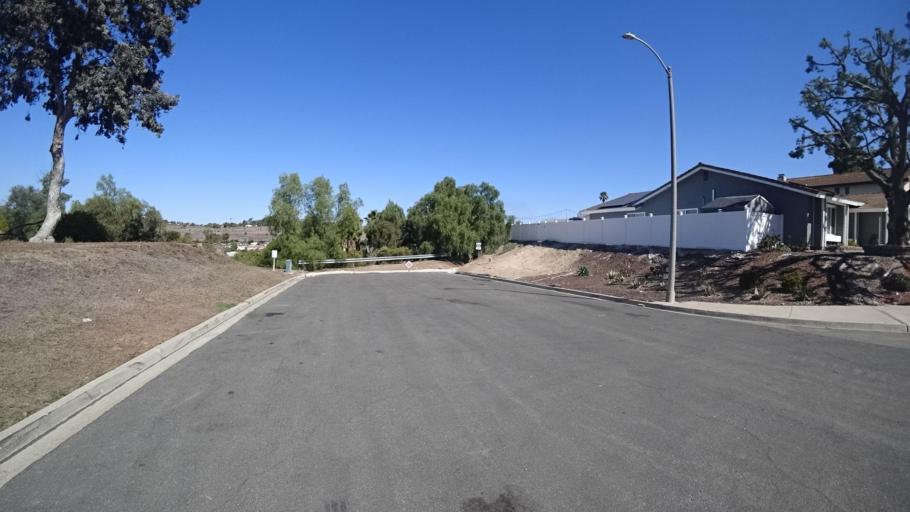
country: US
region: California
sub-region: San Diego County
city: Bonita
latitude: 32.6736
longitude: -117.0036
